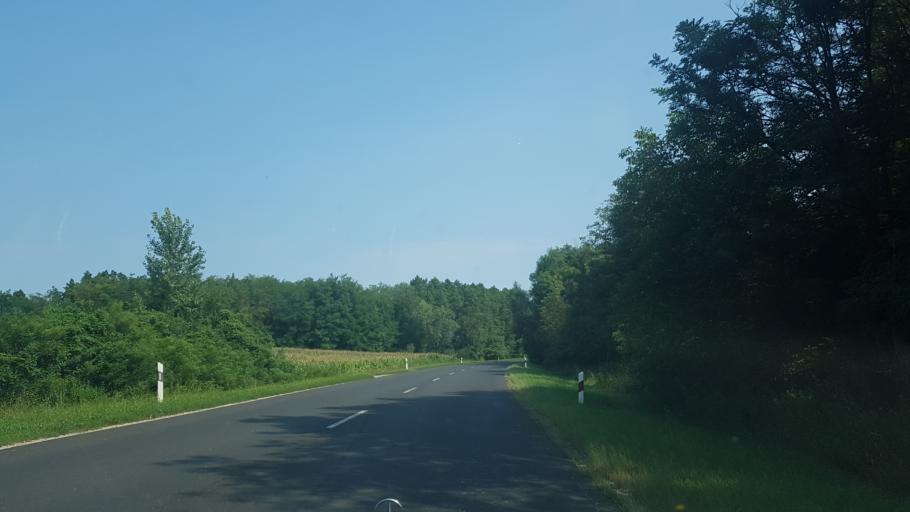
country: HU
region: Somogy
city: Segesd
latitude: 46.3316
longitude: 17.3458
